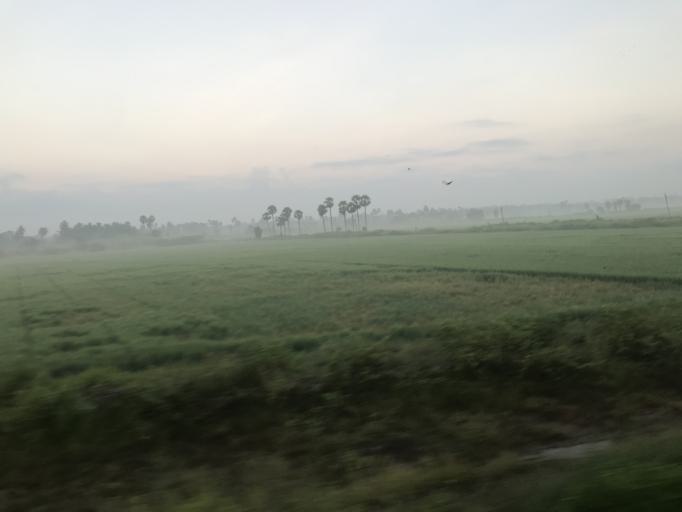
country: IN
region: Andhra Pradesh
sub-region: Guntur
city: Ponnur
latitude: 16.0846
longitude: 80.5649
